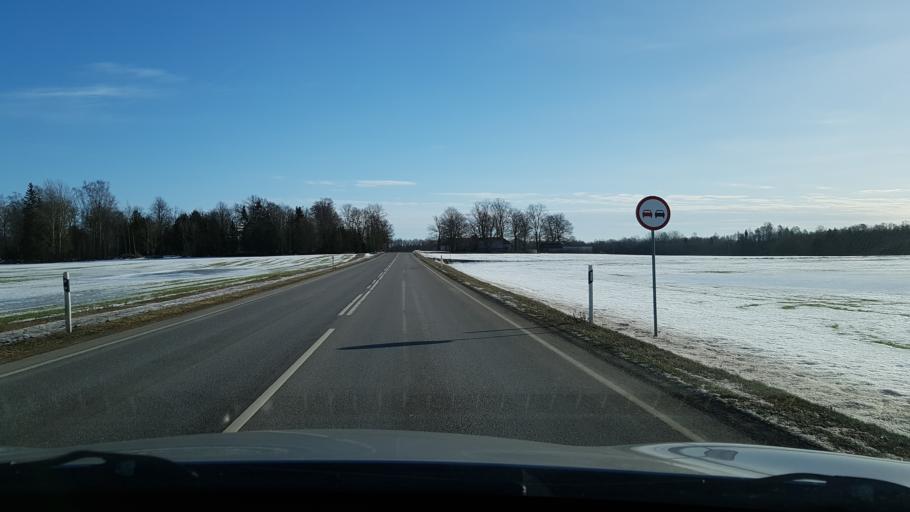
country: EE
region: Viljandimaa
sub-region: Vohma linn
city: Vohma
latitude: 58.6386
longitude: 25.6781
